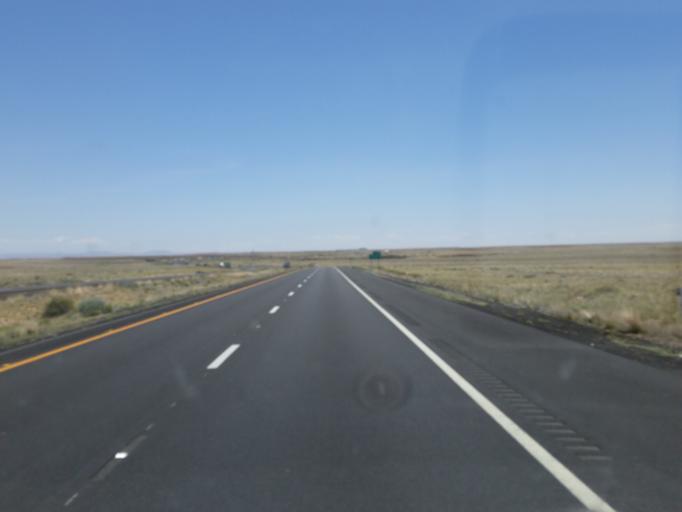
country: US
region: Arizona
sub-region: Coconino County
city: LeChee
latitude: 35.1166
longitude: -111.1147
